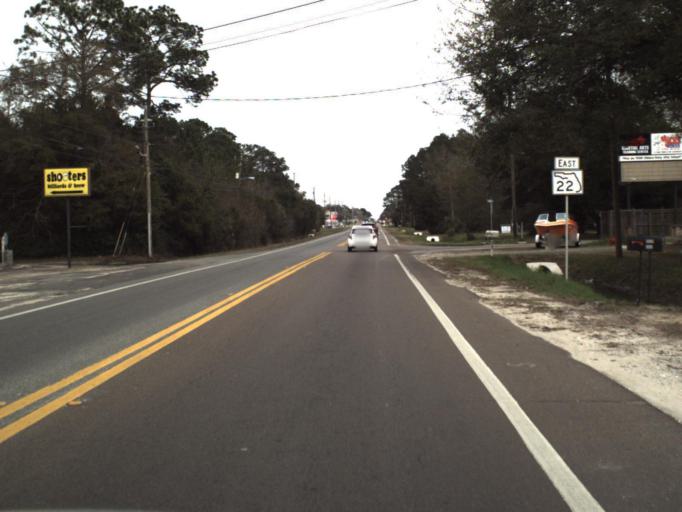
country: US
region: Florida
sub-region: Bay County
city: Springfield
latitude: 30.1530
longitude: -85.5981
